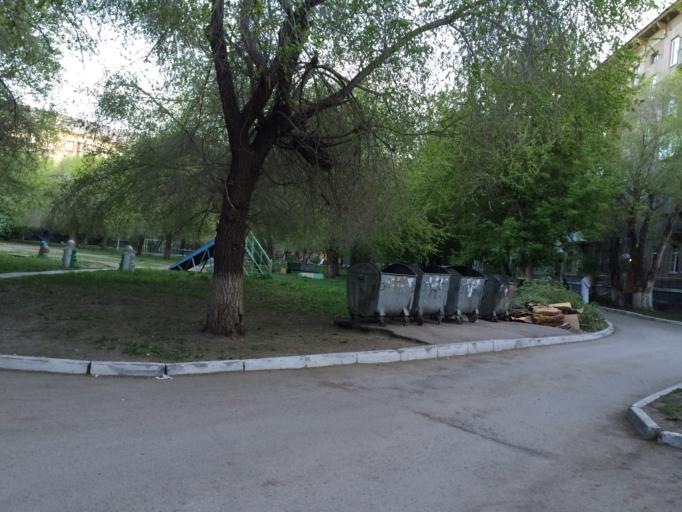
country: RU
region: Chelyabinsk
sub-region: Gorod Magnitogorsk
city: Magnitogorsk
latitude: 53.4131
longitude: 58.9866
